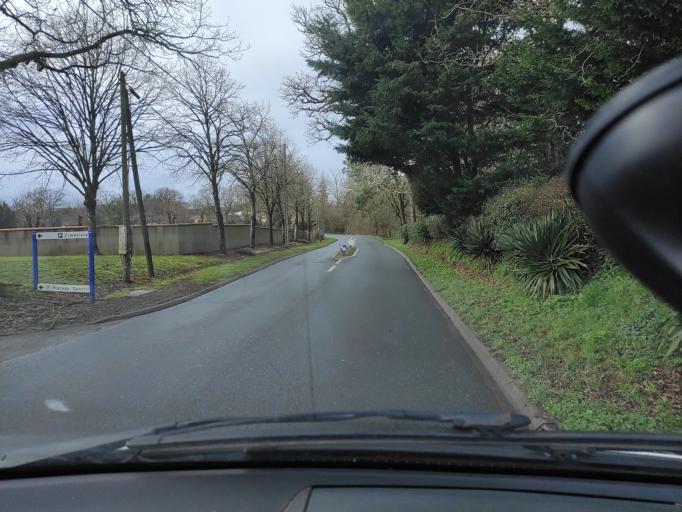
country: FR
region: Pays de la Loire
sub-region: Departement de la Vendee
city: La Boissiere-des-Landes
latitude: 46.5649
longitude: -1.4629
